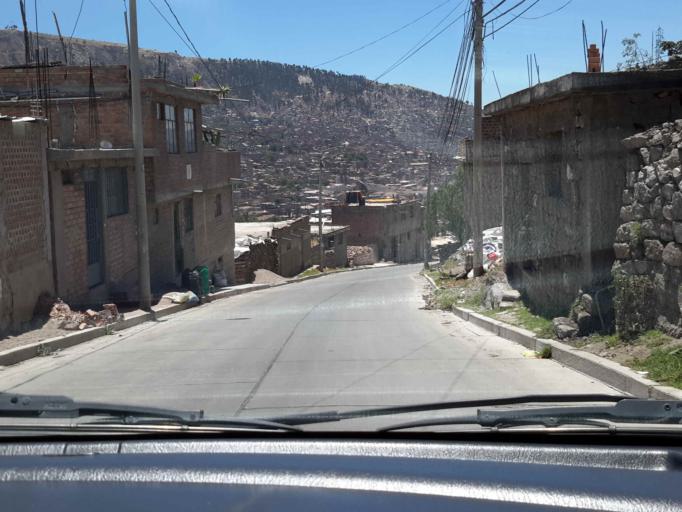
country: PE
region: Ayacucho
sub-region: Provincia de Huamanga
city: Carmen Alto
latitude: -13.1721
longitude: -74.2243
